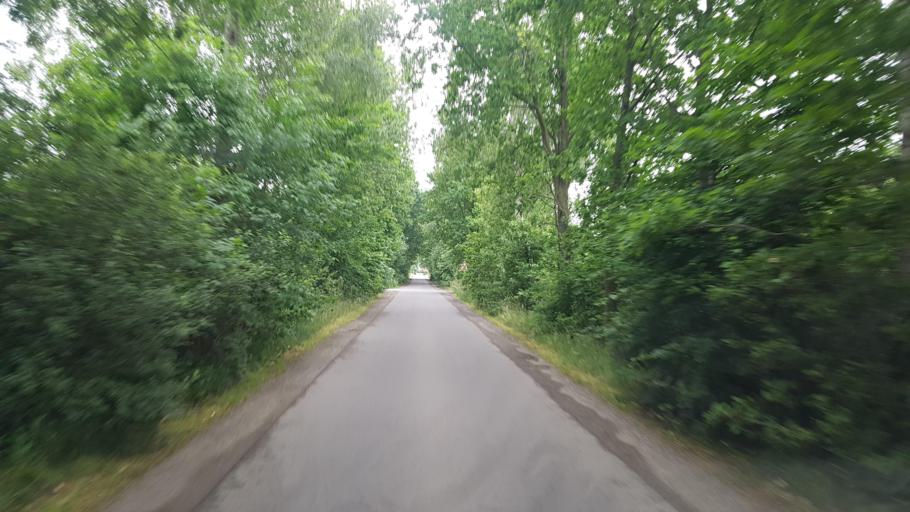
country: DE
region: Brandenburg
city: Schraden
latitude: 51.4292
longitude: 13.6942
